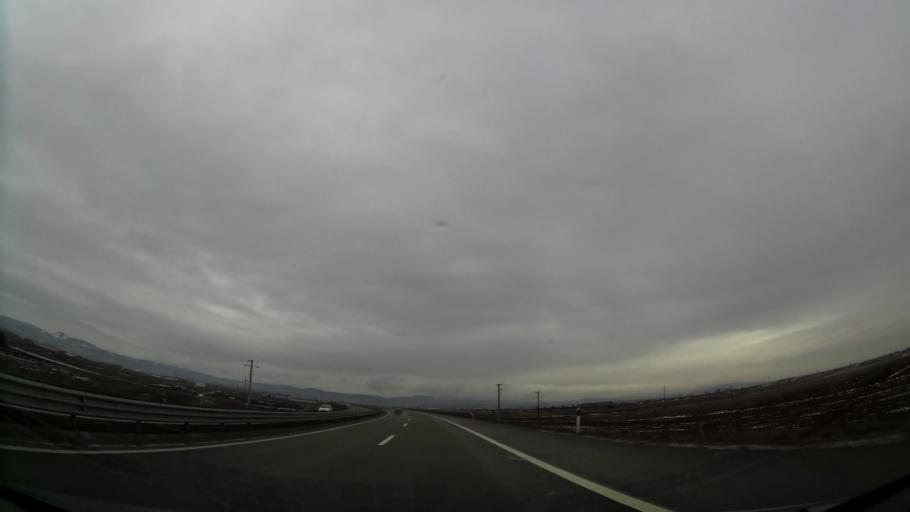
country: XK
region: Pristina
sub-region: Lipjan
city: Lipljan
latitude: 42.5307
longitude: 21.1450
